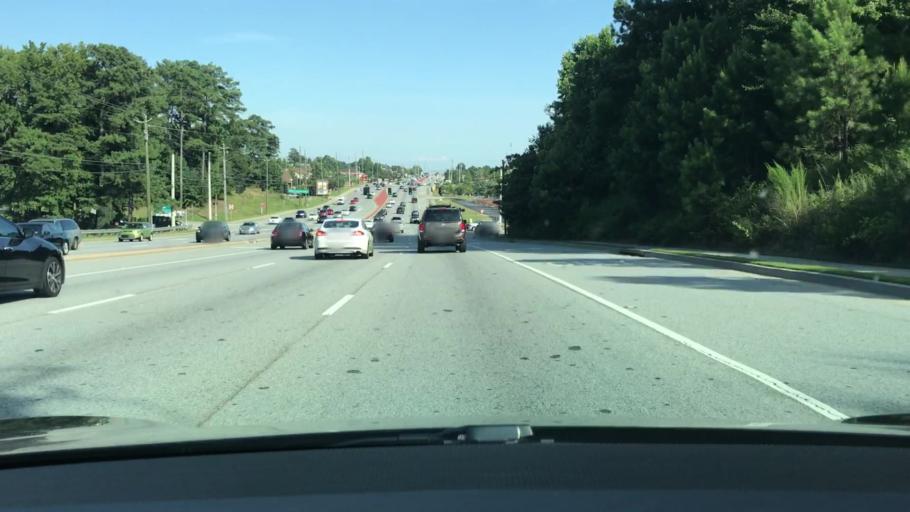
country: US
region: Georgia
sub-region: Gwinnett County
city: Duluth
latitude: 33.9730
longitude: -84.1507
